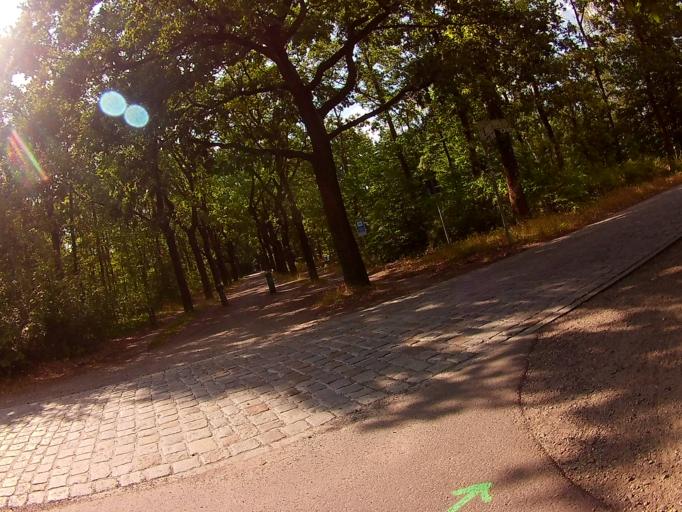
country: DE
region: Berlin
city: Oberschoneweide
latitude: 52.4657
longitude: 13.5299
